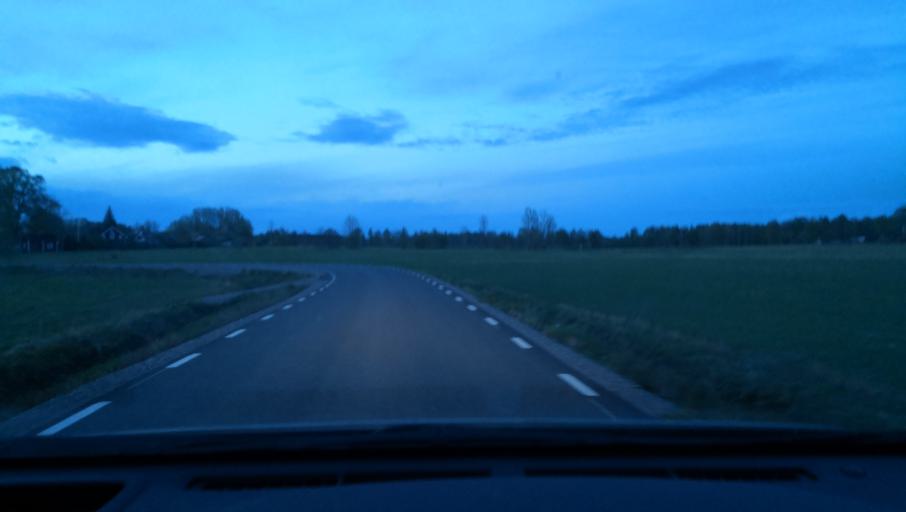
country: SE
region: OErebro
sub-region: Askersunds Kommun
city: Asbro
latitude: 59.0631
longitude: 14.9498
